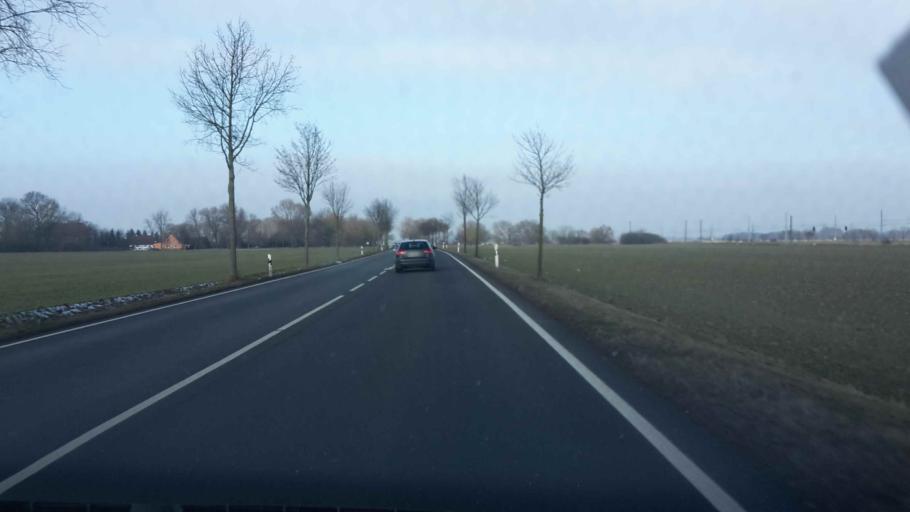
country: DE
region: Saxony-Anhalt
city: Seehausen
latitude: 52.9120
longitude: 11.7346
